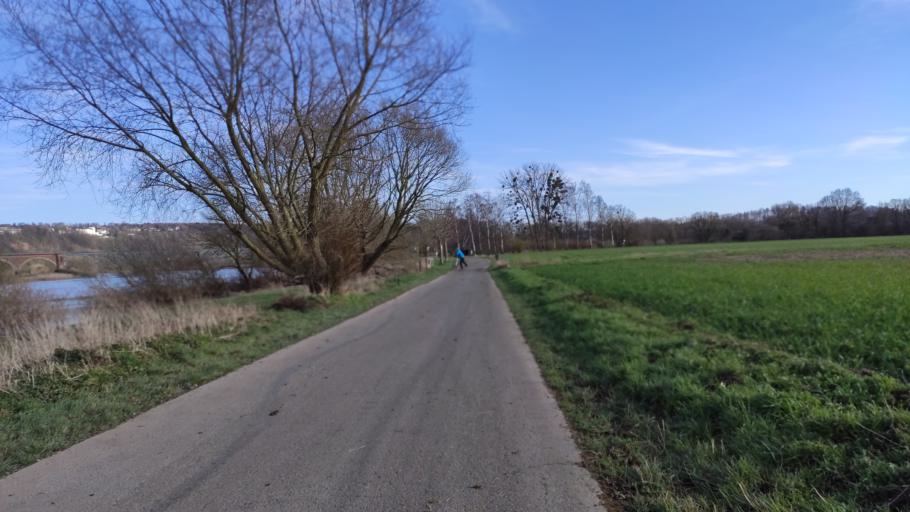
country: DE
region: Lower Saxony
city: Boffzen
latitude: 51.7392
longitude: 9.3762
